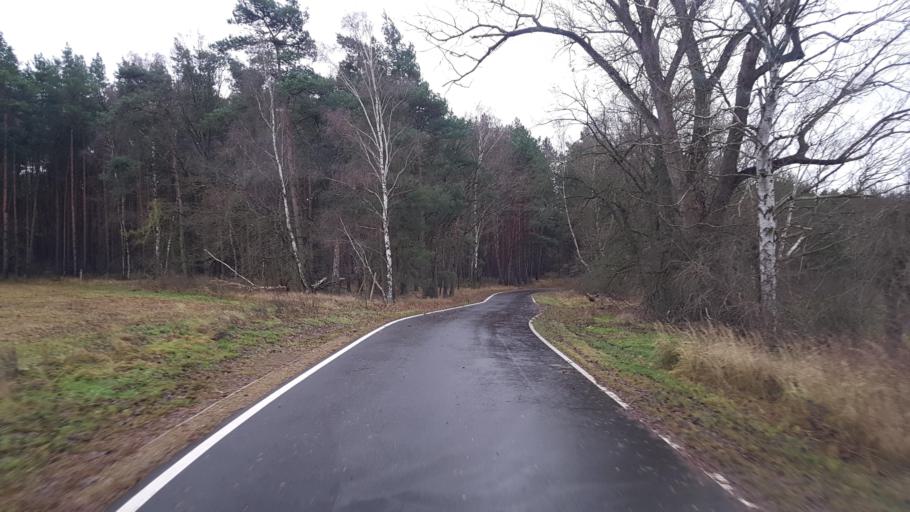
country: DE
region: Brandenburg
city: Tauche
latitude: 52.1024
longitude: 14.1188
